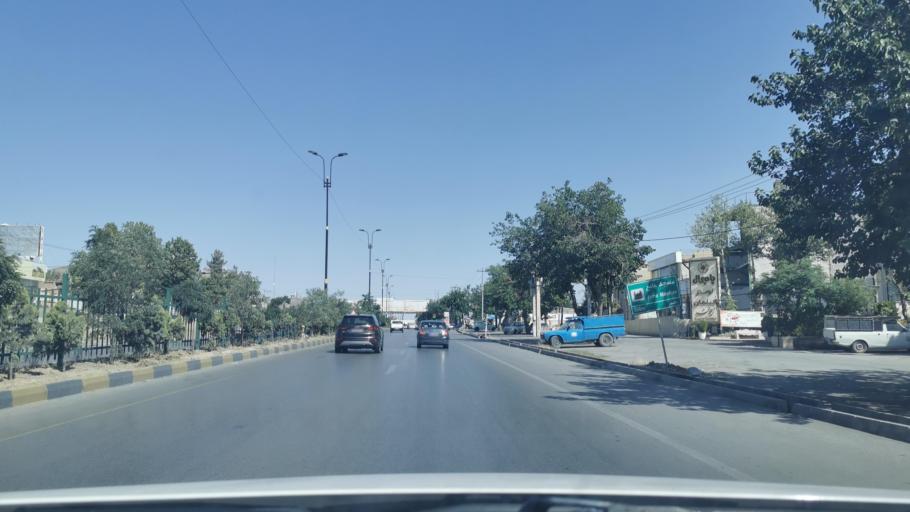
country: IR
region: Razavi Khorasan
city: Torqabeh
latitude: 36.3968
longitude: 59.3955
